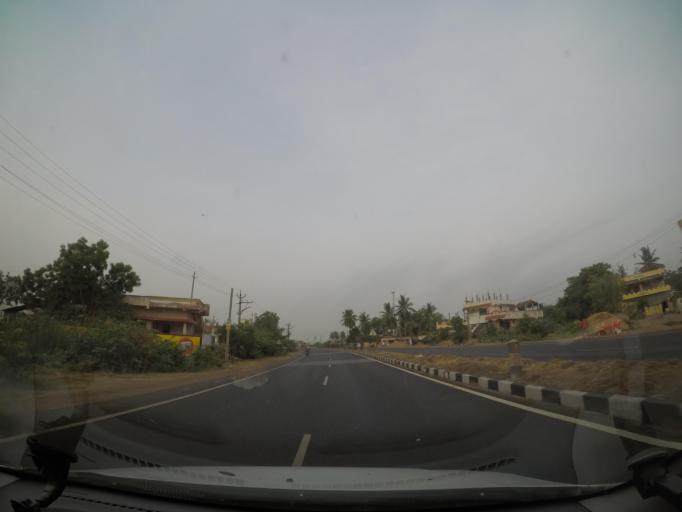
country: IN
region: Andhra Pradesh
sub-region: Krishna
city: Gannavaram
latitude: 16.5983
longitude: 80.8943
